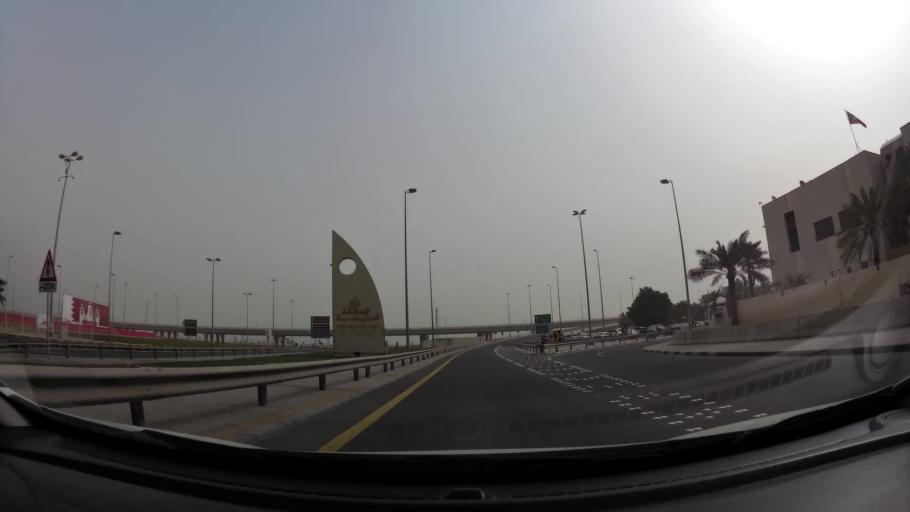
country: BH
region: Muharraq
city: Al Muharraq
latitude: 26.2442
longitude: 50.5882
